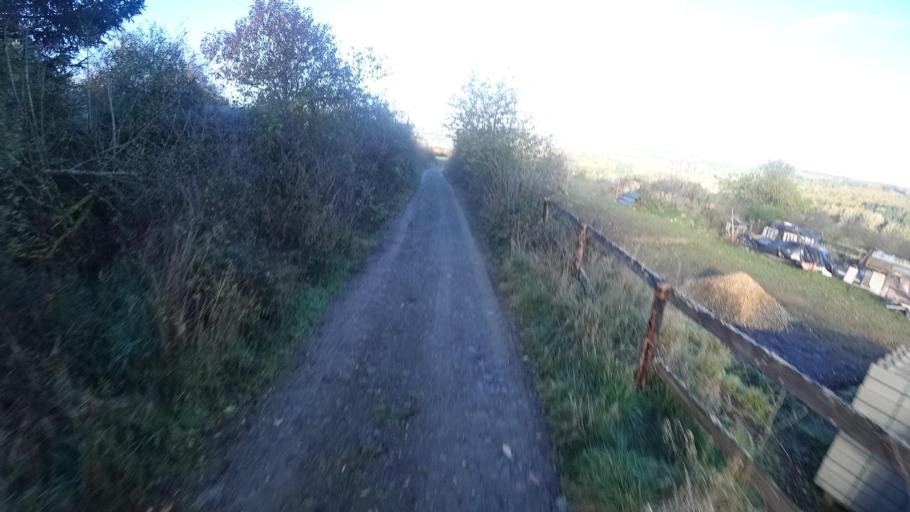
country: DE
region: Rheinland-Pfalz
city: Kirchsahr
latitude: 50.5297
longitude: 6.9257
